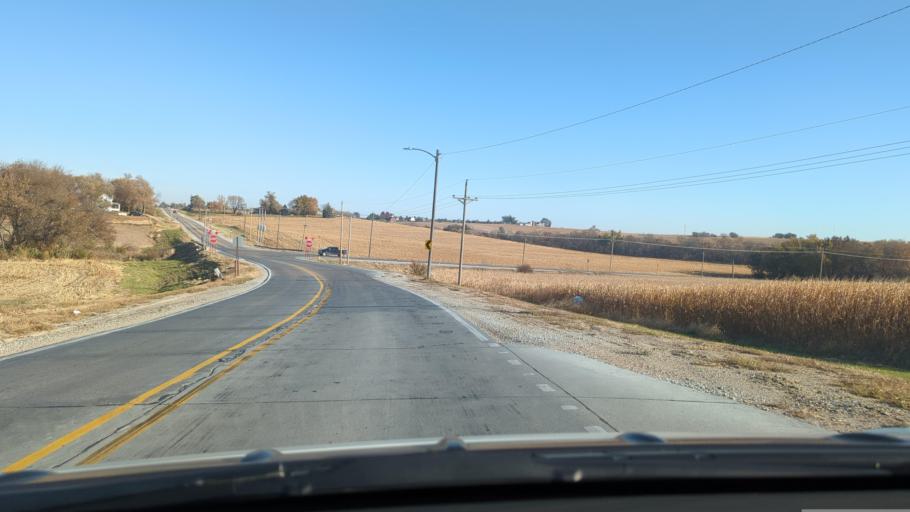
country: US
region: Nebraska
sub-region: Sarpy County
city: Papillion
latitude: 41.0910
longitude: -96.0433
